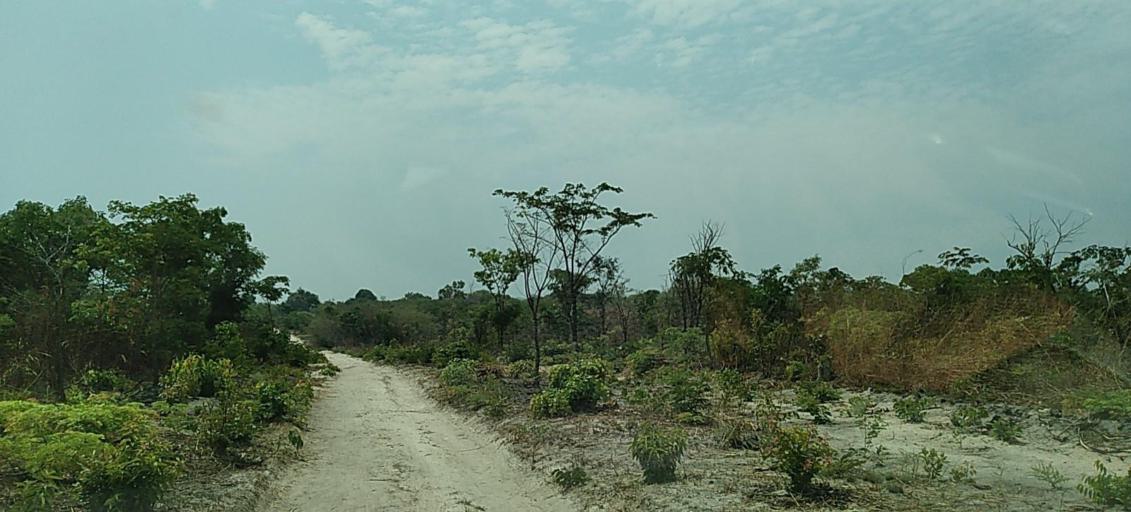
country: ZM
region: Copperbelt
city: Kalulushi
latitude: -12.9409
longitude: 28.1182
